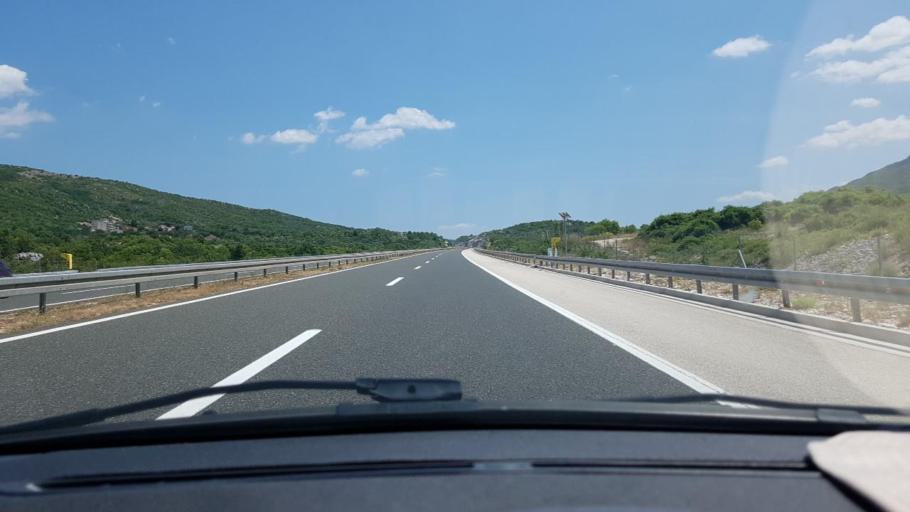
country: HR
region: Splitsko-Dalmatinska
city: Grubine
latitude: 43.3857
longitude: 17.0662
